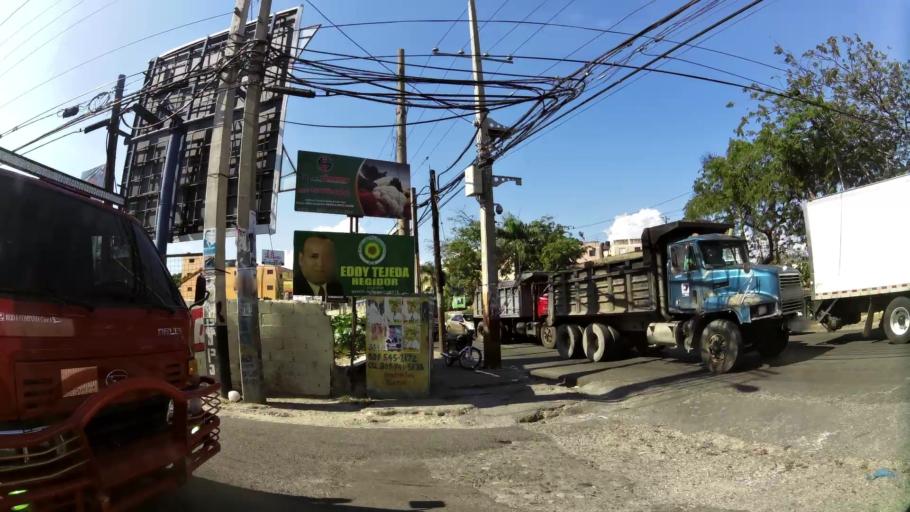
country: DO
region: Santo Domingo
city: Santo Domingo Oeste
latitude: 18.4647
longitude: -69.9943
